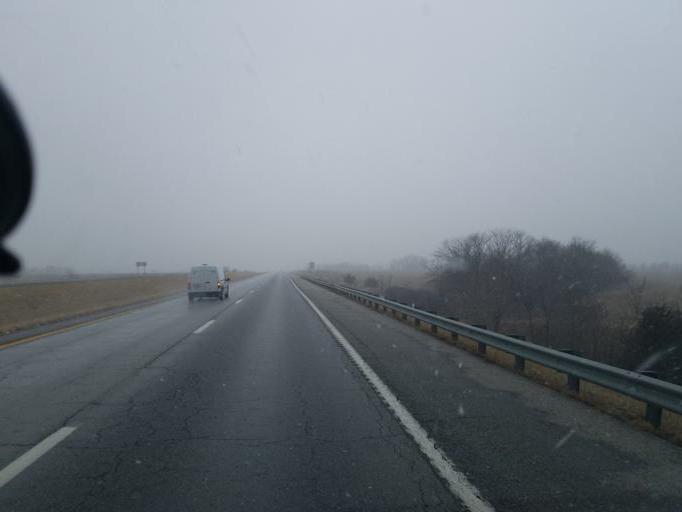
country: US
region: Missouri
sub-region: Macon County
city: La Plata
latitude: 39.9835
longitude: -92.4759
